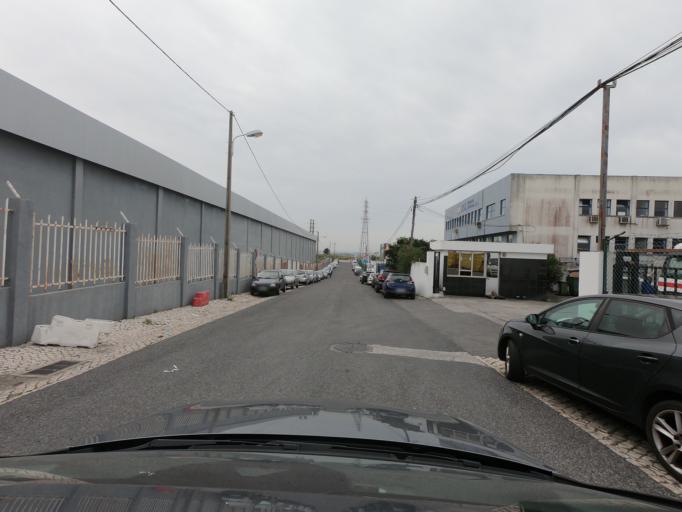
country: PT
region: Lisbon
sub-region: Oeiras
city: Barcarena
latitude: 38.7386
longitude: -9.2673
